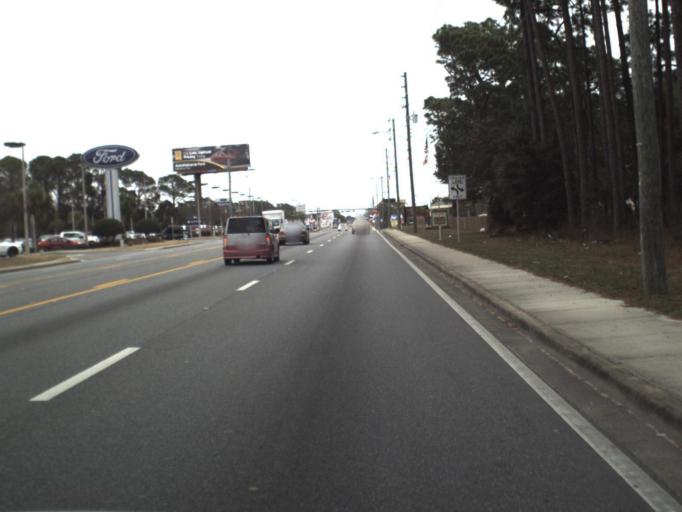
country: US
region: Florida
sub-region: Bay County
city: Panama City
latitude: 30.1752
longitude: -85.6720
